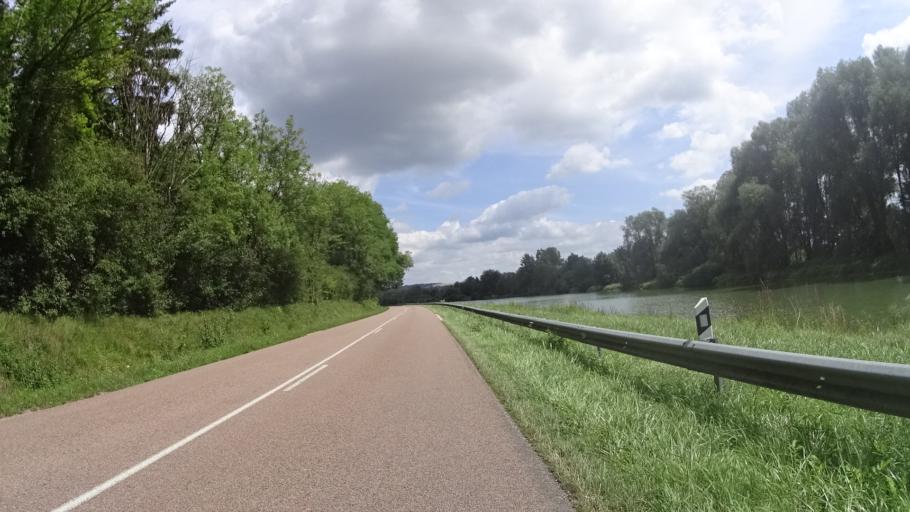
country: FR
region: Lorraine
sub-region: Departement de la Meuse
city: Euville
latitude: 48.7414
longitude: 5.6417
